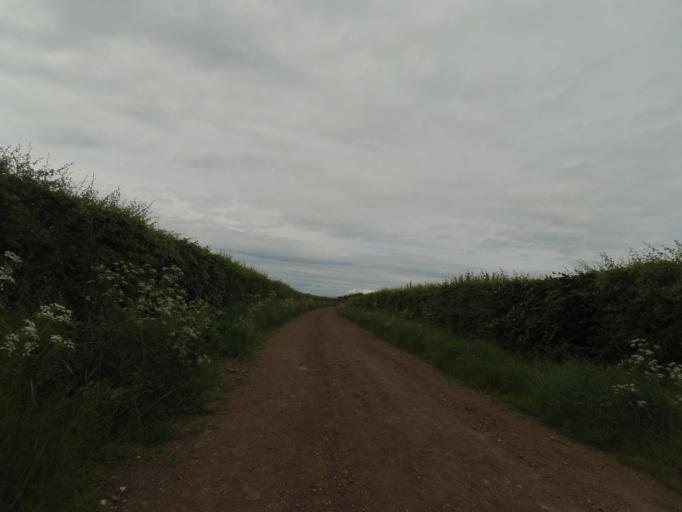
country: GB
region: Scotland
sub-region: East Lothian
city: Macmerry
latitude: 55.9458
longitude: -2.9246
